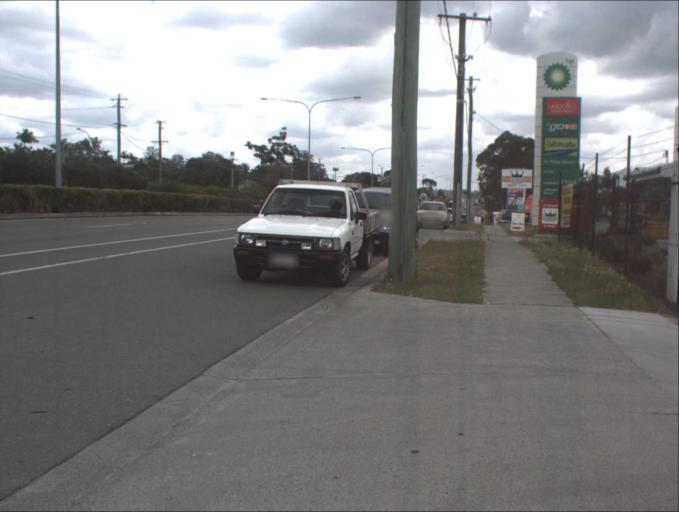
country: AU
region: Queensland
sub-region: Logan
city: Beenleigh
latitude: -27.7144
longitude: 153.1909
